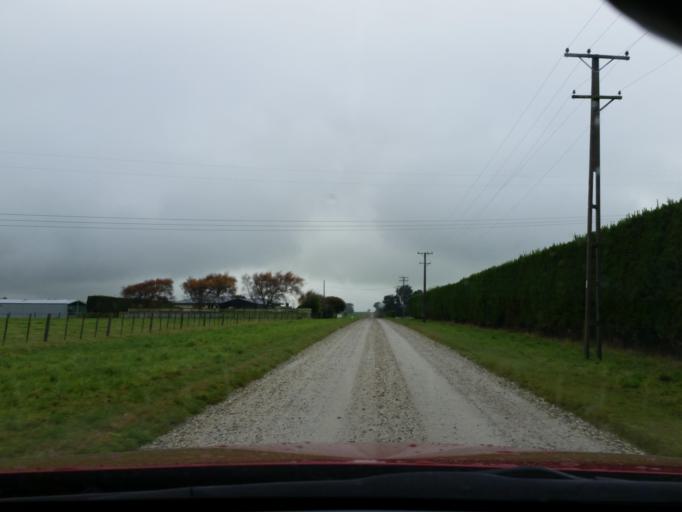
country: NZ
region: Southland
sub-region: Invercargill City
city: Invercargill
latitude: -46.2953
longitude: 168.5564
